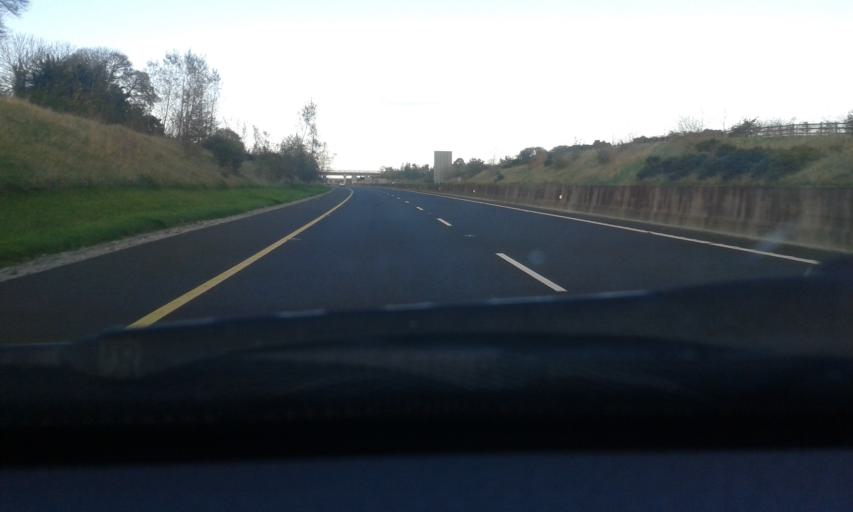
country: IE
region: Munster
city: Thurles
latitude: 52.6283
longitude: -7.7677
